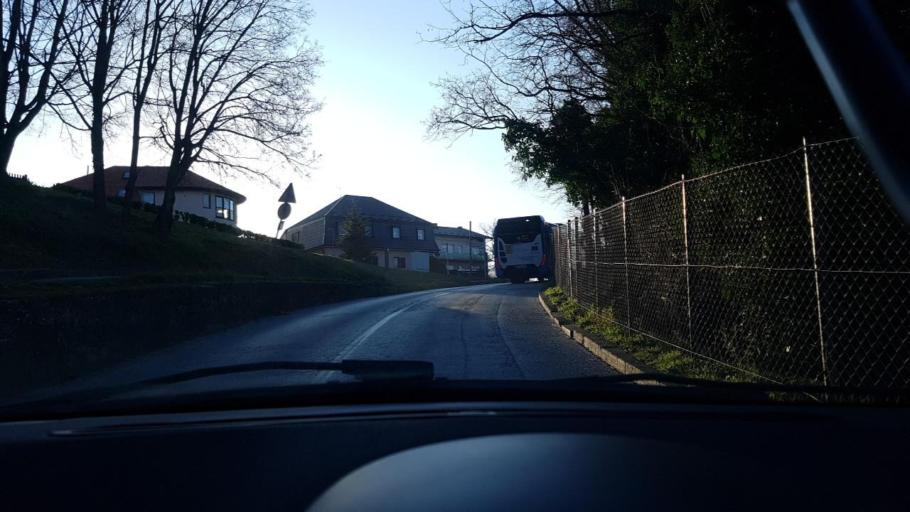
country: HR
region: Grad Zagreb
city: Zagreb
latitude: 45.8509
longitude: 15.9928
